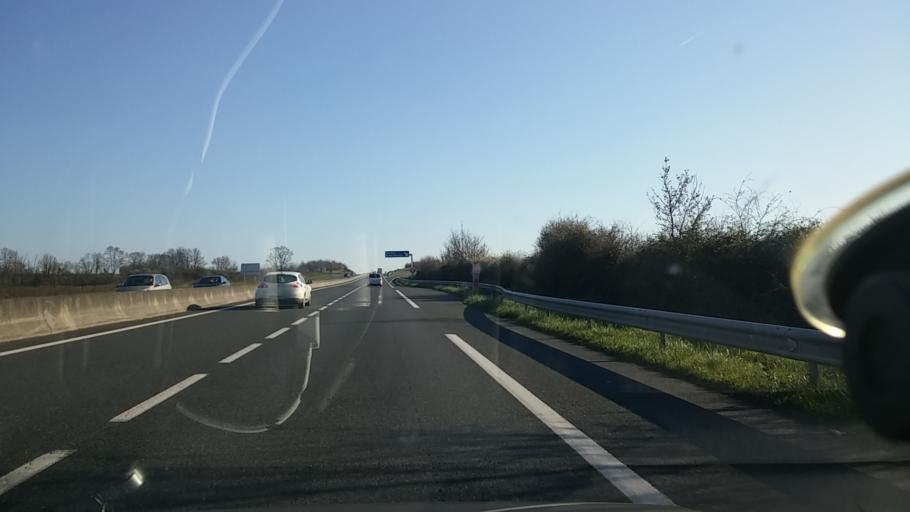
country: FR
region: Centre
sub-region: Departement de l'Indre
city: Argenton-sur-Creuse
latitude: 46.5533
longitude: 1.5060
